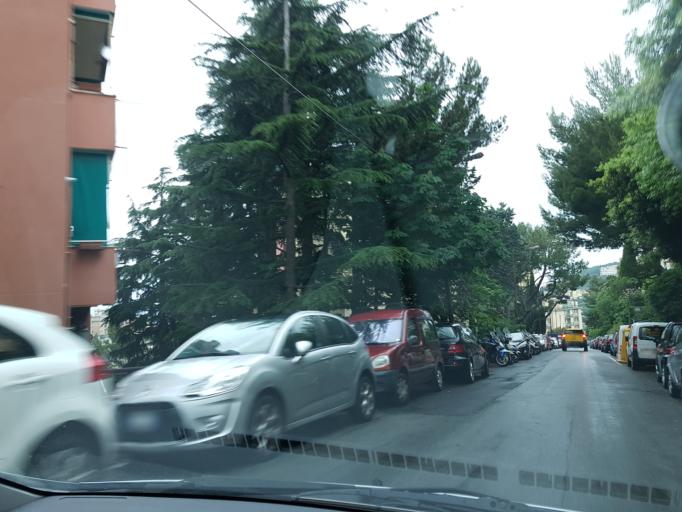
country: IT
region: Liguria
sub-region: Provincia di Genova
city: Genoa
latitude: 44.4272
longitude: 8.9223
